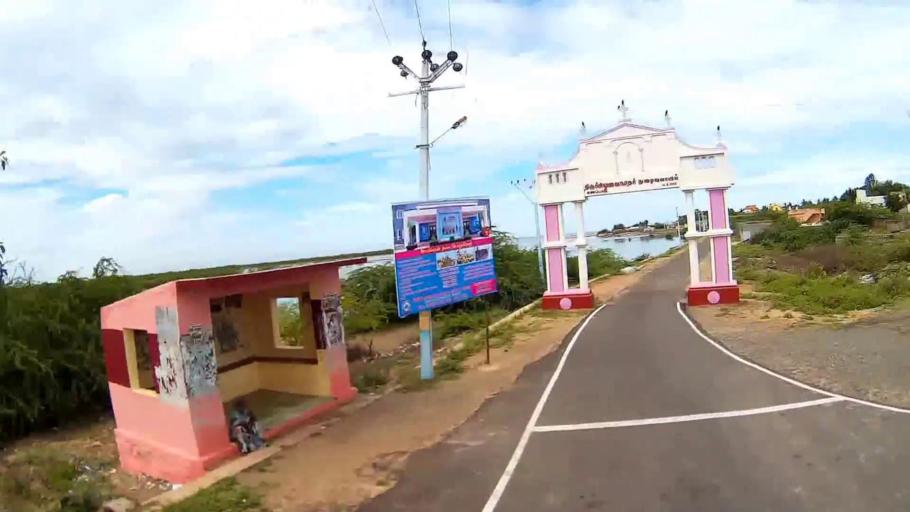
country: IN
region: Tamil Nadu
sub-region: Thoothukkudi
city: Udankudi
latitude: 8.3789
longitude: 78.0511
